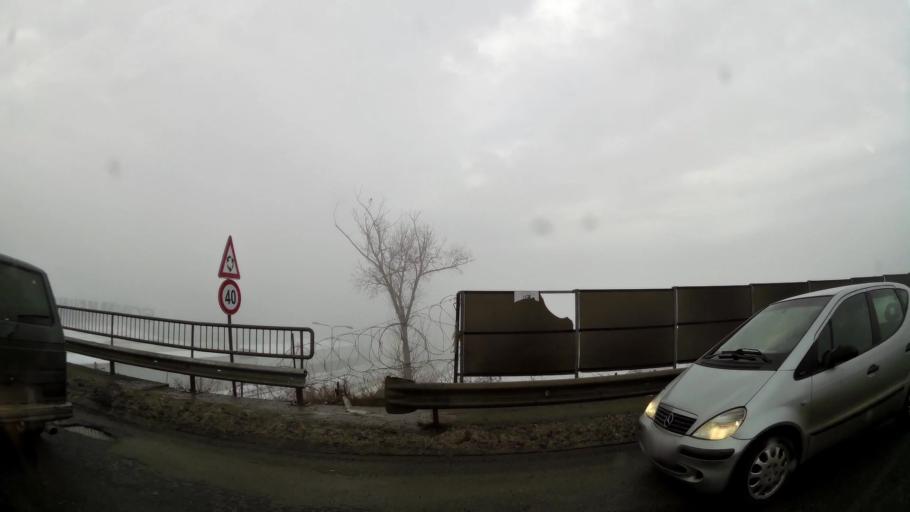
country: XK
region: Pristina
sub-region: Komuna e Prishtines
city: Pristina
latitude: 42.6532
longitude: 21.1445
